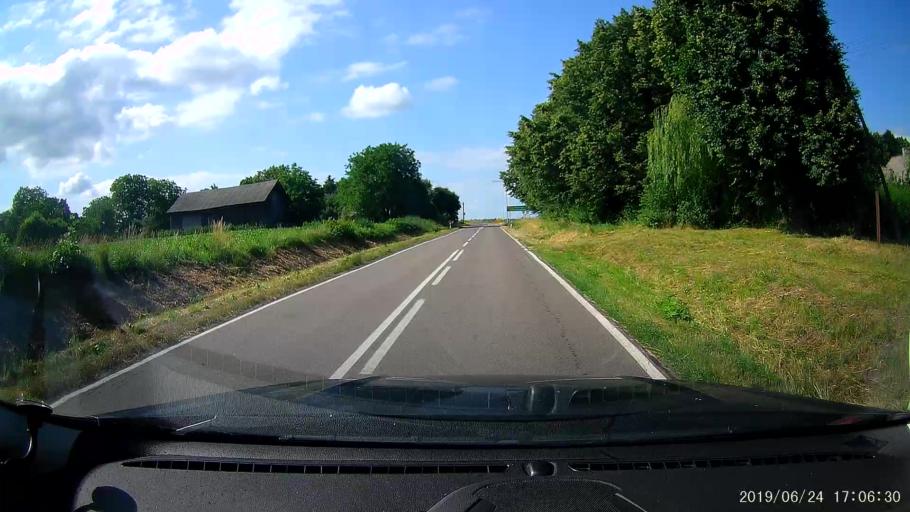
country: PL
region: Lublin Voivodeship
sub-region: Powiat hrubieszowski
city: Dolhobyczow
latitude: 50.5875
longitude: 23.9712
